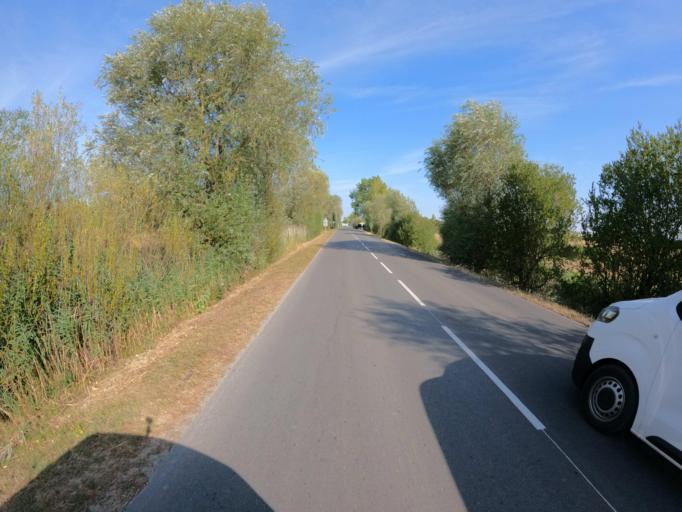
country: FR
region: Pays de la Loire
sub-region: Departement de la Vendee
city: Le Perrier
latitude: 46.8131
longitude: -1.9890
